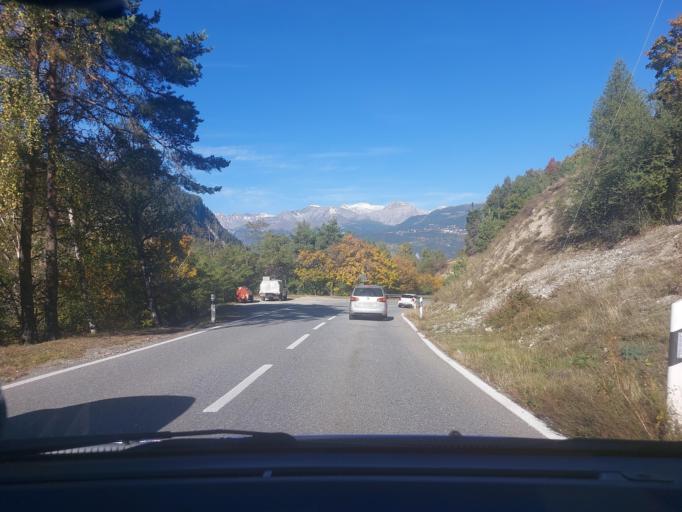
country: CH
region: Valais
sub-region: Sierre District
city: Chippis
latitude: 46.2592
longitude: 7.5663
